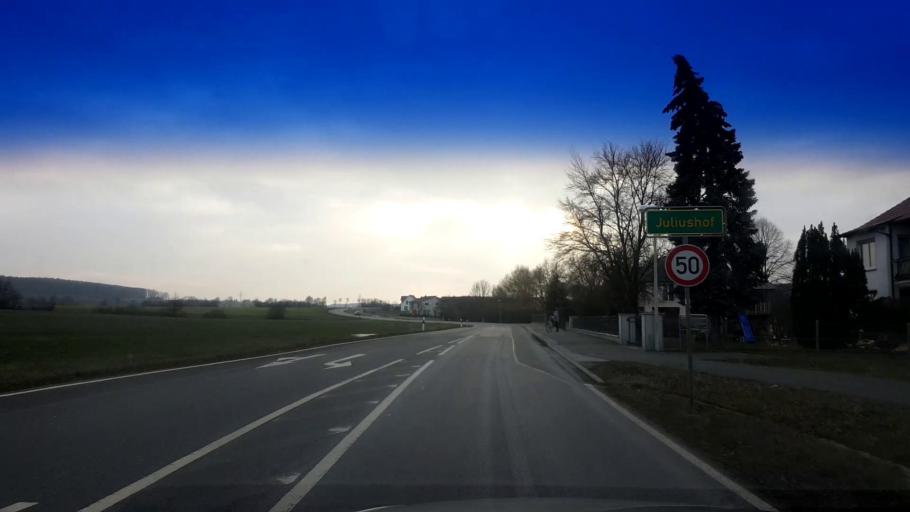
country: DE
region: Bavaria
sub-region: Upper Franconia
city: Hirschaid
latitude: 49.8022
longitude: 10.9748
